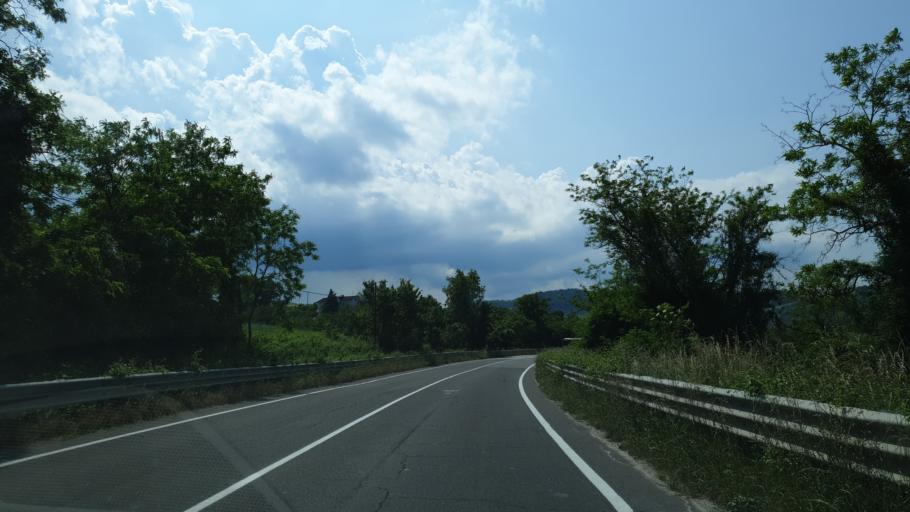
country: IT
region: Emilia-Romagna
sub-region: Provincia di Rimini
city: Pietracuta
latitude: 43.9569
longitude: 12.3907
